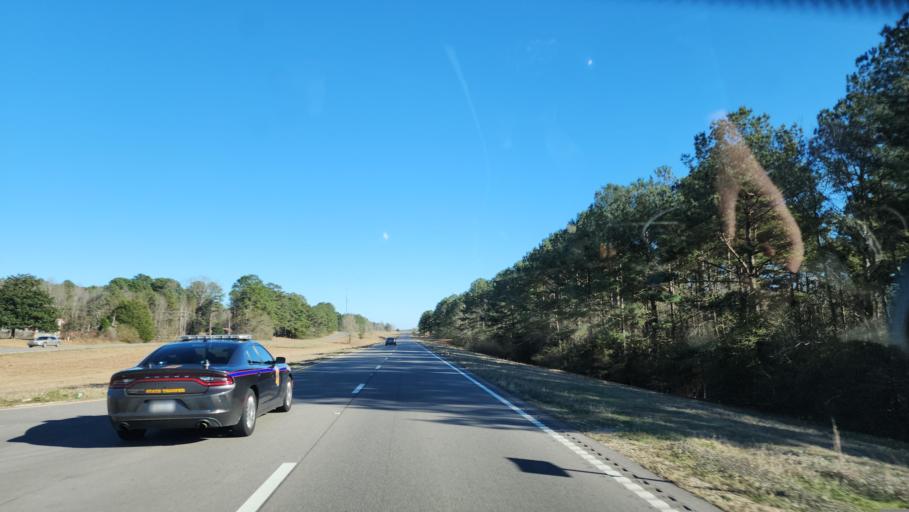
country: US
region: Mississippi
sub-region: Jones County
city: Sharon
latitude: 31.7059
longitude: -88.9348
